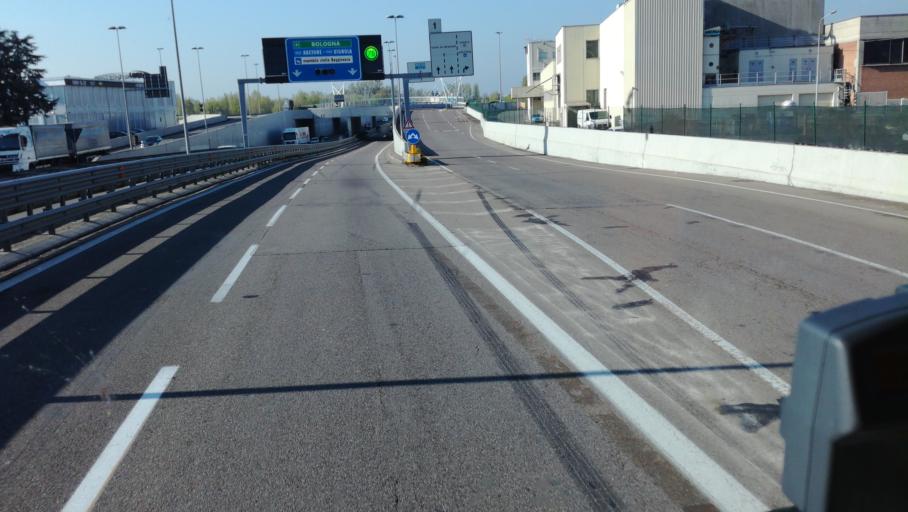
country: IT
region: Emilia-Romagna
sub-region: Provincia di Modena
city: Modena
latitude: 44.6349
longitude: 10.9581
